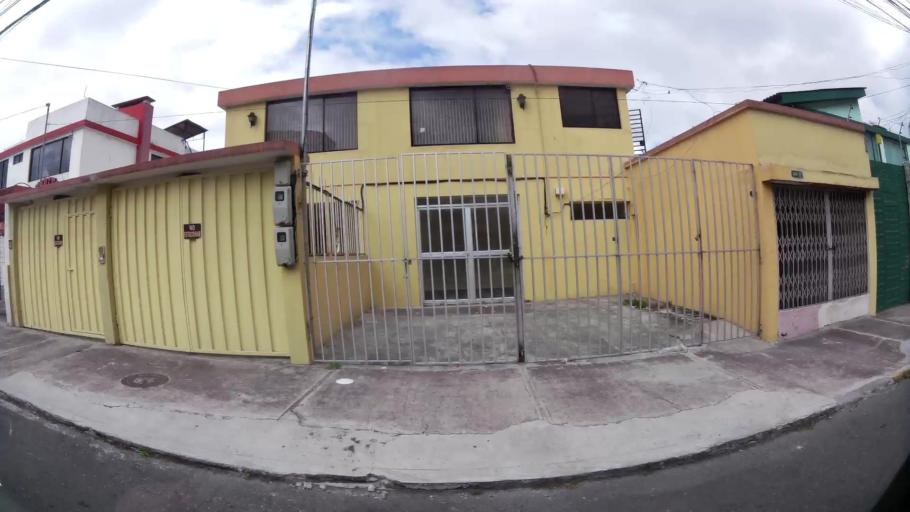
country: EC
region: Pichincha
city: Quito
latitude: -0.1511
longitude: -78.4926
